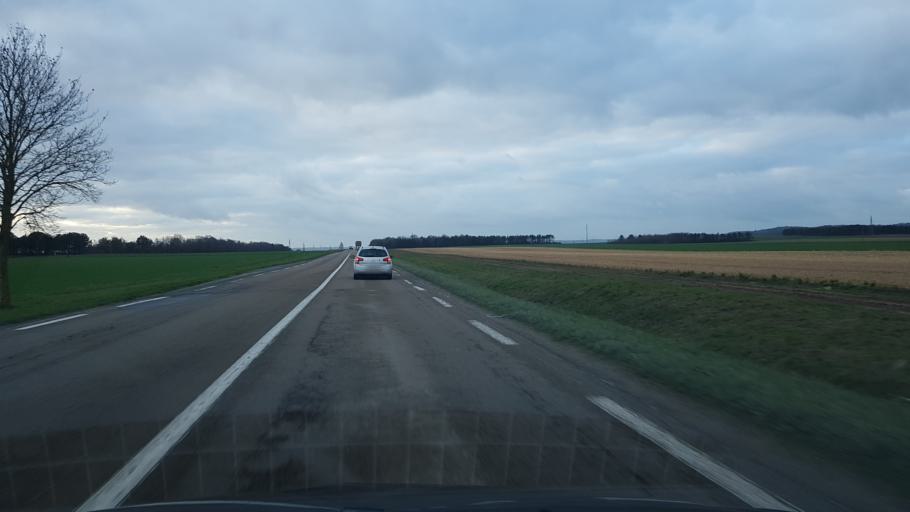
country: FR
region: Champagne-Ardenne
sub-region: Departement de la Marne
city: Connantre
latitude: 48.7288
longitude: 3.8904
